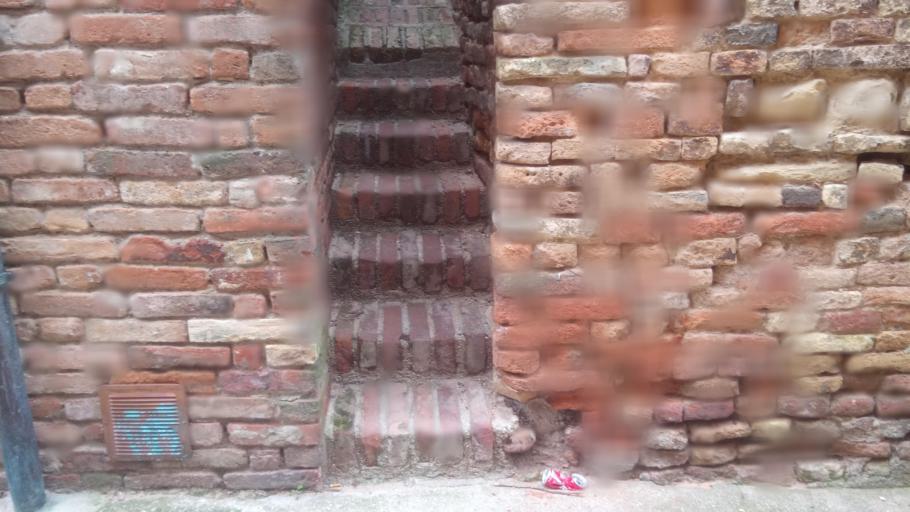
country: IT
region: The Marches
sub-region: Provincia di Ascoli Piceno
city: Ripatransone
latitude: 43.0002
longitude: 13.7625
